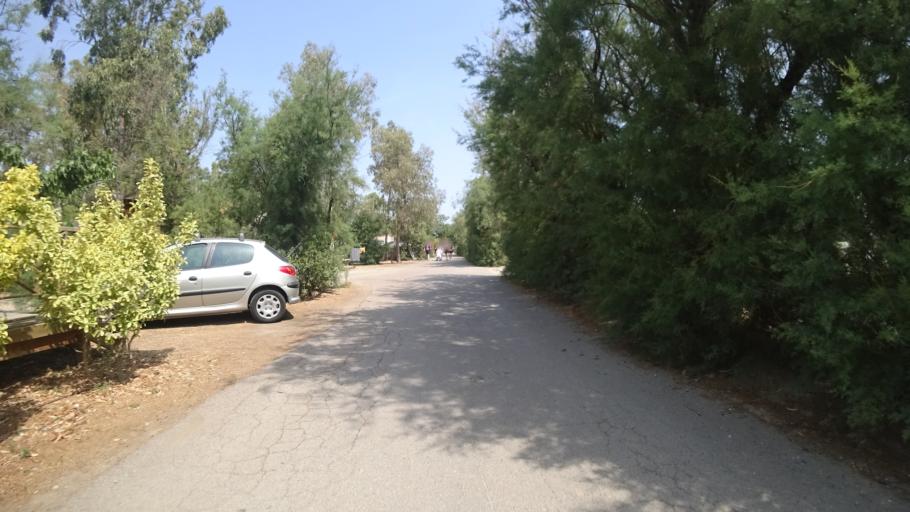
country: FR
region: Languedoc-Roussillon
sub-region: Departement des Pyrenees-Orientales
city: Le Barcares
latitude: 42.7852
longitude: 3.0256
